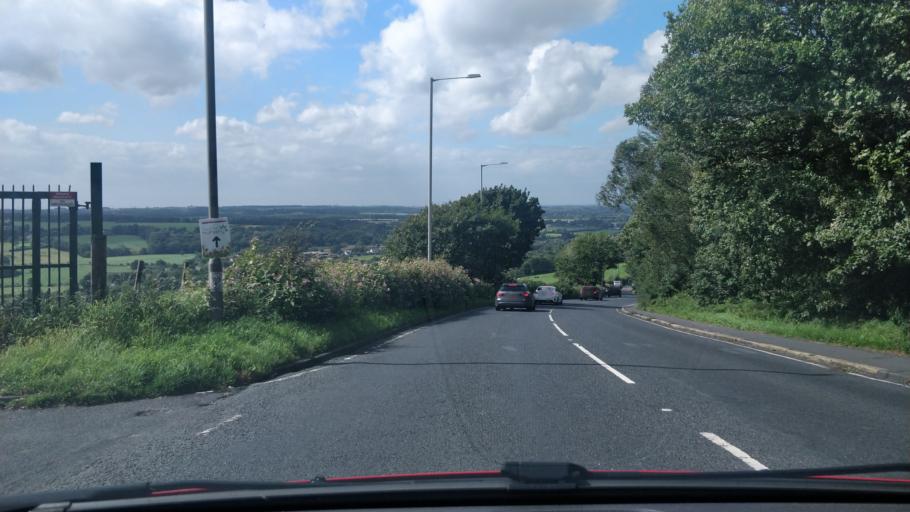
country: GB
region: England
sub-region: Lancashire
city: Parbold
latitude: 53.5902
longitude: -2.7494
